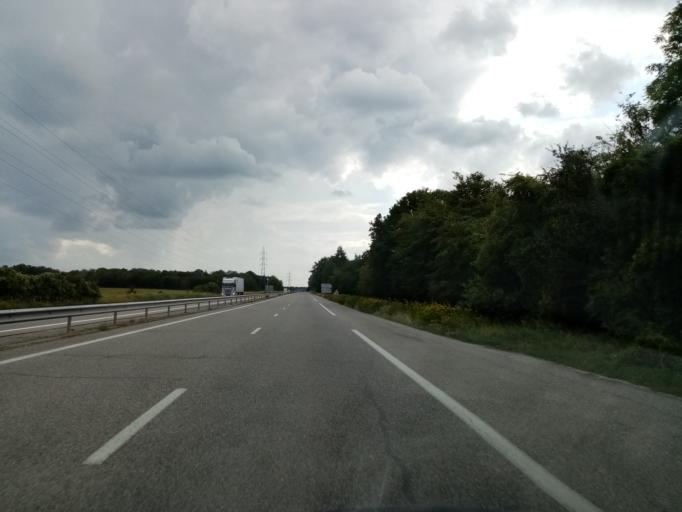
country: FR
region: Alsace
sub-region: Departement du Bas-Rhin
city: Soufflenheim
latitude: 48.8179
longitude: 7.9930
